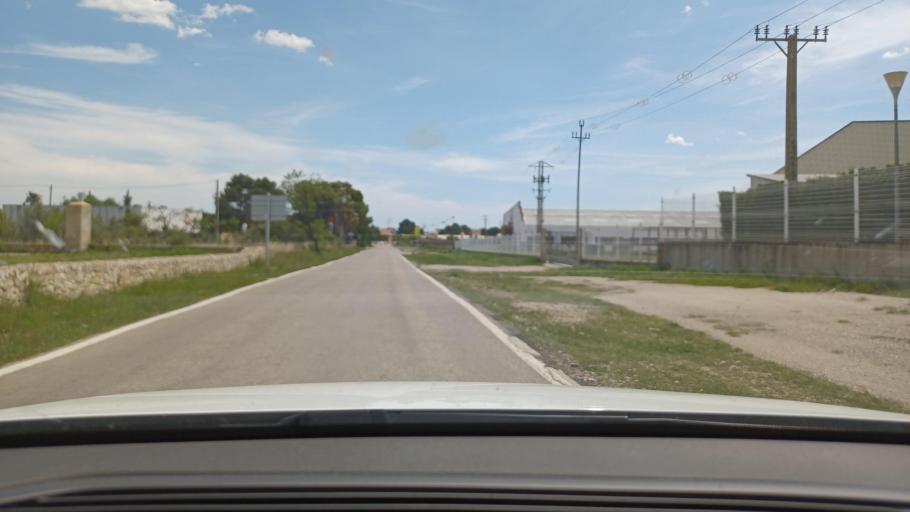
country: ES
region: Valencia
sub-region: Provincia de Castello
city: Rosell
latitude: 40.6430
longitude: 0.2745
